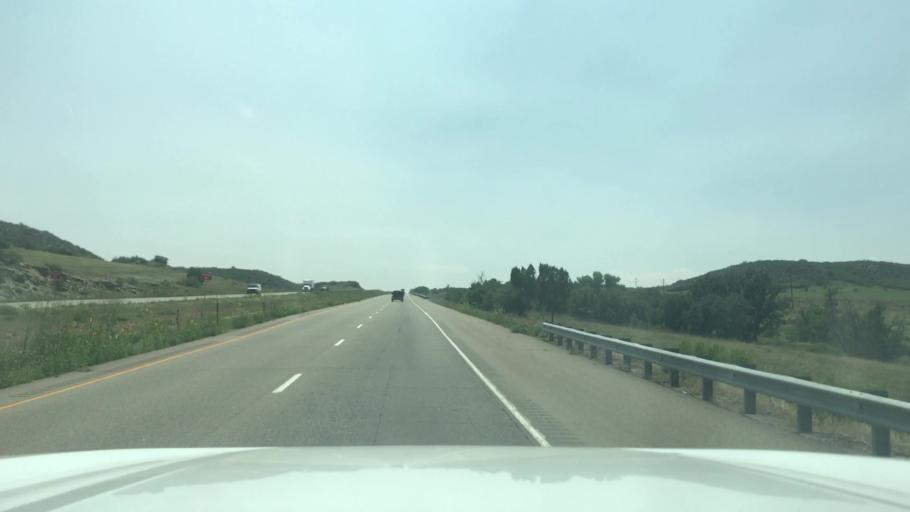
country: US
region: Colorado
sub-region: Pueblo County
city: Colorado City
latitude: 37.9076
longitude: -104.8292
